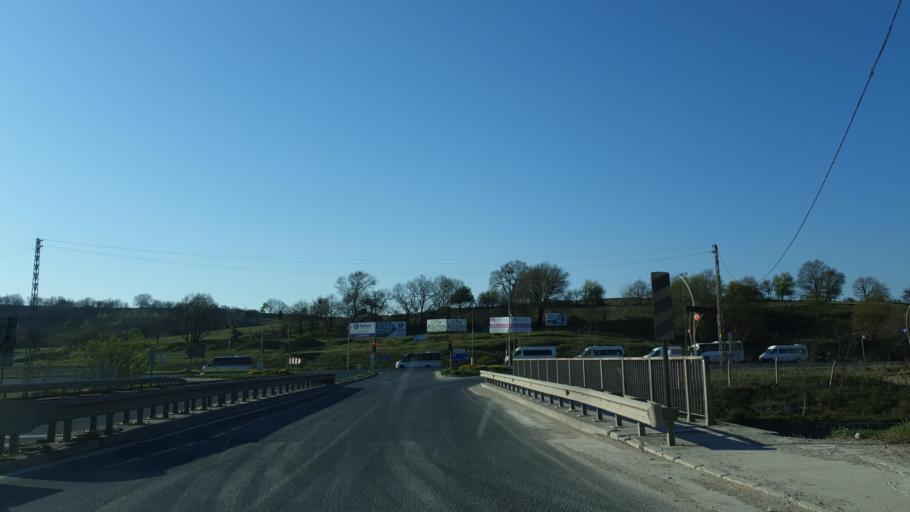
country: TR
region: Tekirdag
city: Cerkezkoey
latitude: 41.2763
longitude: 27.9863
